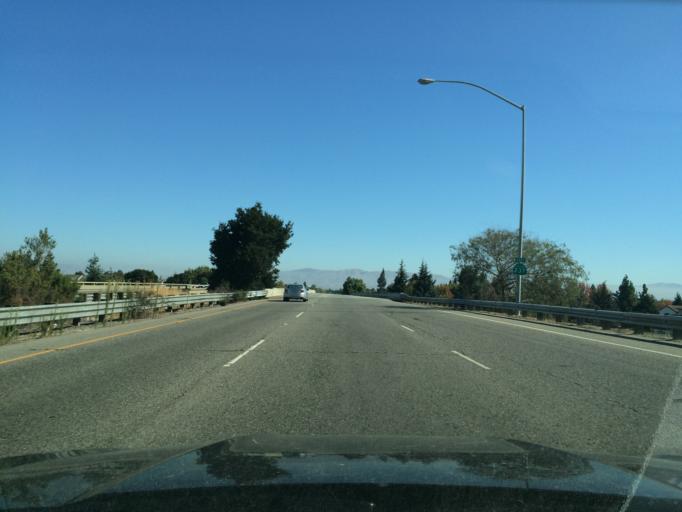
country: US
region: California
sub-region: Santa Clara County
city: Mountain View
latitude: 37.3866
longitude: -122.0589
